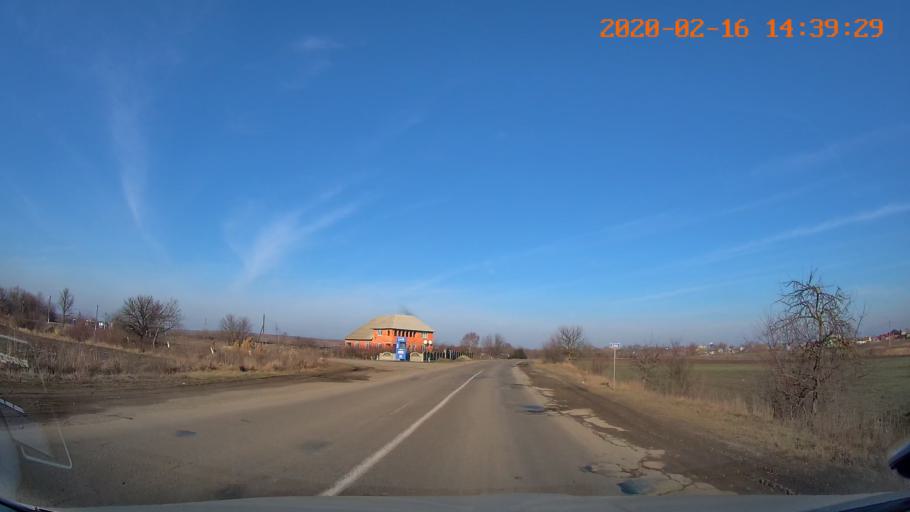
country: RO
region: Botosani
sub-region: Comuna Darabani
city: Bajura
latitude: 48.2437
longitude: 26.5494
